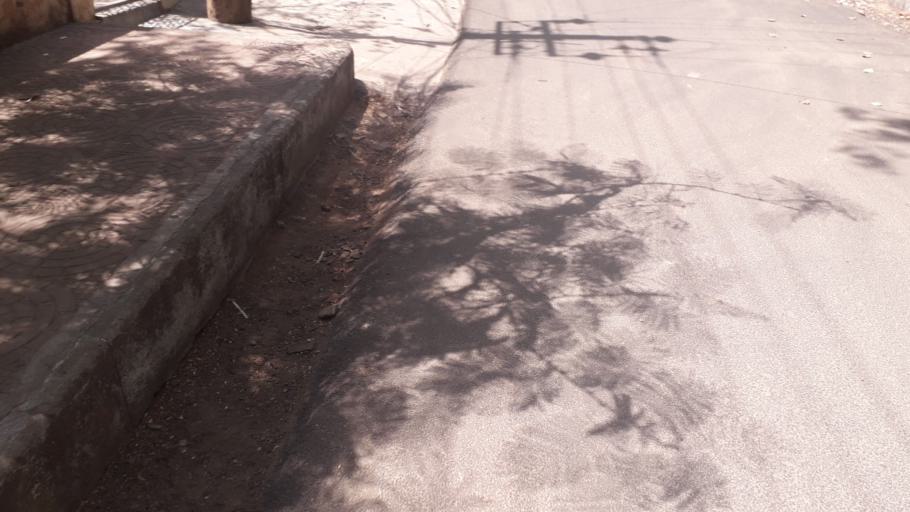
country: IN
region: Telangana
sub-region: Rangareddi
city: Kukatpalli
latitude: 17.4433
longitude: 78.4431
